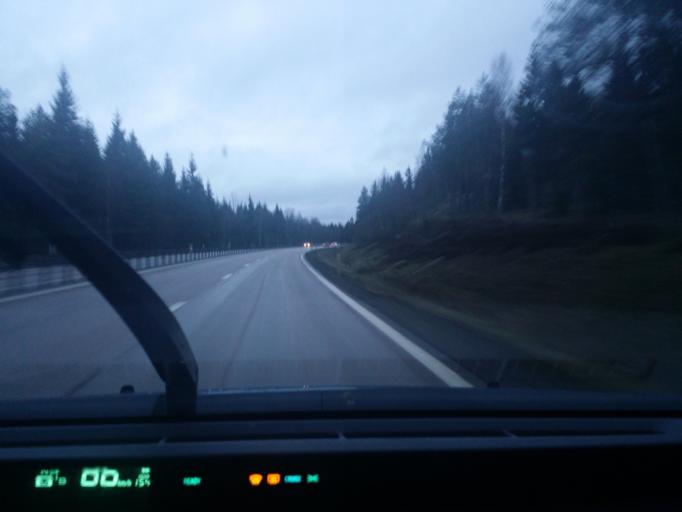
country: SE
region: Soedermanland
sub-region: Eskilstuna Kommun
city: Hallbybrunn
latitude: 59.4127
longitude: 16.3682
